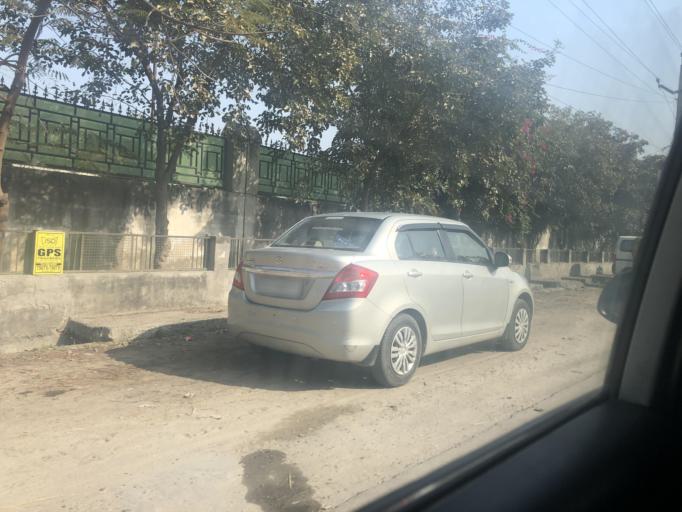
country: IN
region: Haryana
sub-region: Jhajjar
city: Bahadurgarh
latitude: 28.6870
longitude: 76.8908
